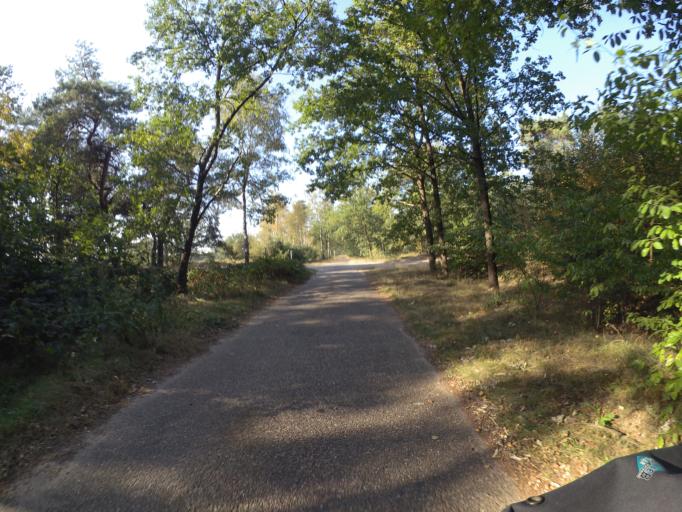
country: NL
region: North Brabant
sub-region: Gemeente Oirschot
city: Oirschot
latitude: 51.4773
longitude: 5.3271
